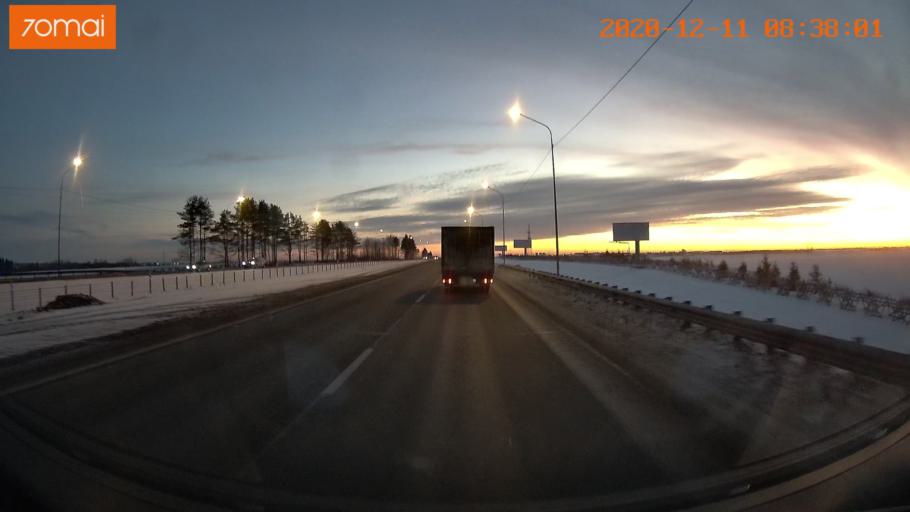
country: RU
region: Vologda
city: Molochnoye
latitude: 59.2109
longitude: 39.7203
